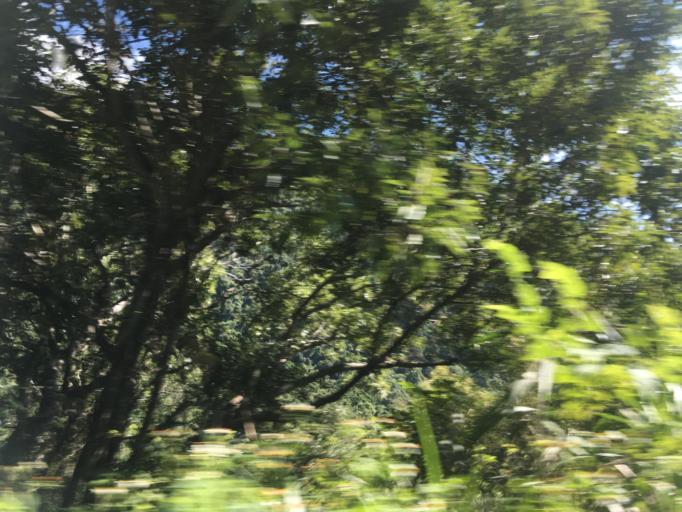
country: TW
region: Taiwan
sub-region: Yilan
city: Yilan
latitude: 24.4203
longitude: 121.7290
